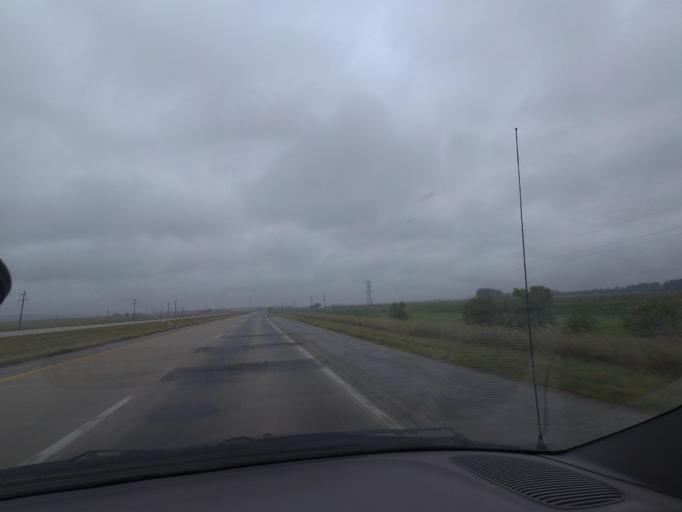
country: US
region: Illinois
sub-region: Adams County
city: Payson
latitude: 39.7297
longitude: -91.2340
